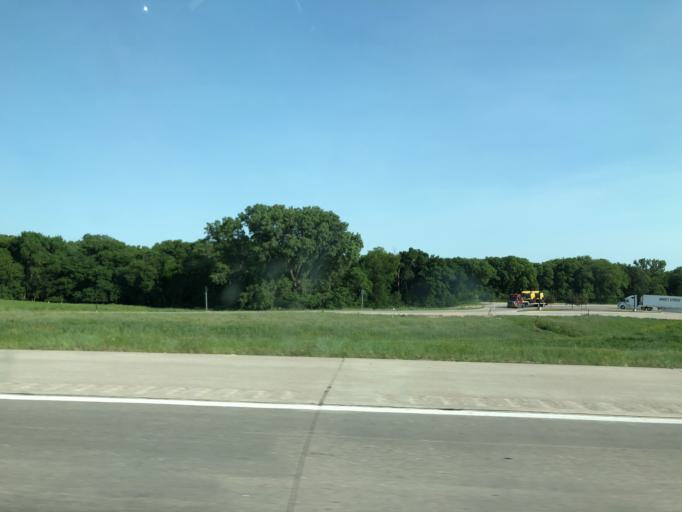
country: US
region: Nebraska
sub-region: Saunders County
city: Ashland
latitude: 41.0040
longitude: -96.3186
